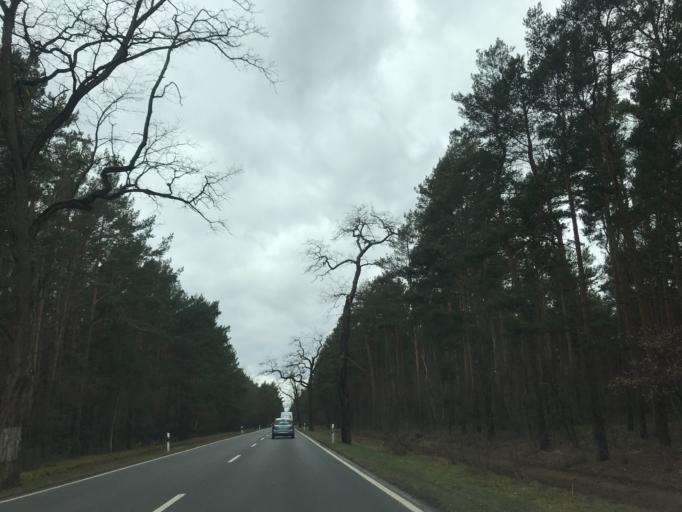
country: DE
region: Brandenburg
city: Luebben
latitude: 51.9471
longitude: 13.8590
